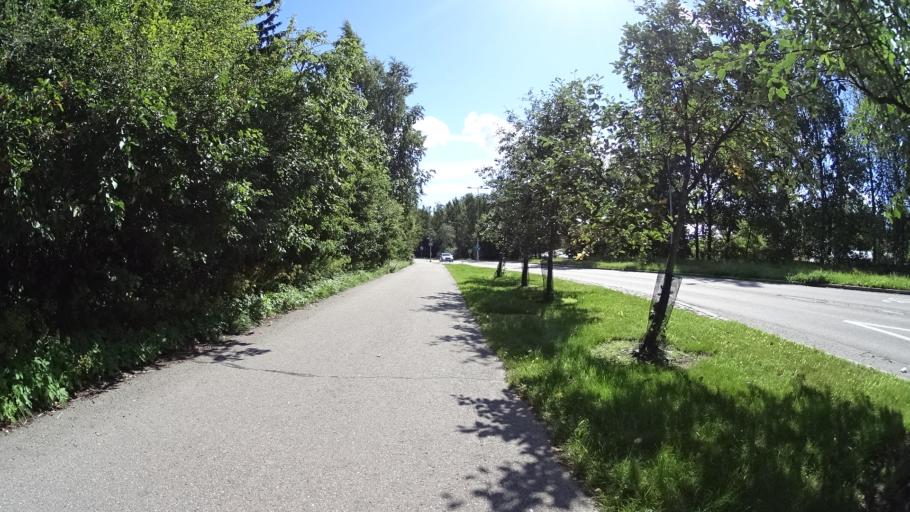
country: FI
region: Uusimaa
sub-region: Helsinki
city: Kauniainen
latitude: 60.2345
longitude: 24.7453
